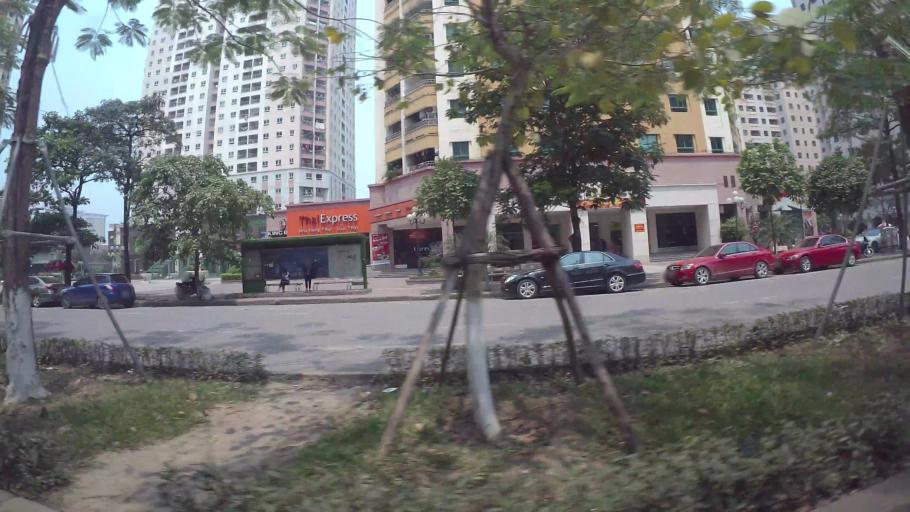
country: VN
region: Ha Noi
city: Thanh Xuan
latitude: 21.0073
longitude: 105.8026
